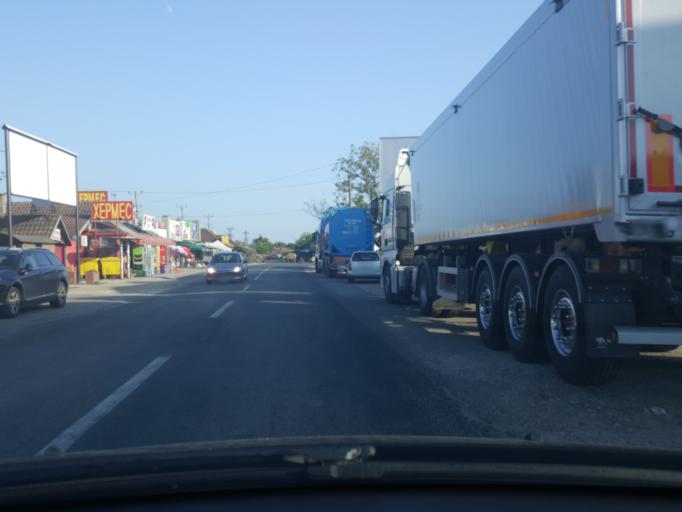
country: RS
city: Platicevo
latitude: 44.8246
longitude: 19.7804
